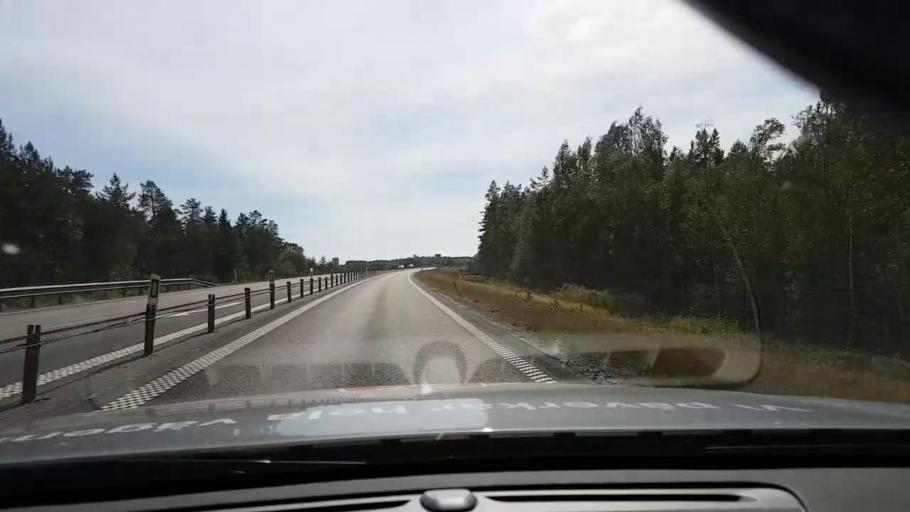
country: SE
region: Vaesternorrland
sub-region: OErnskoeldsviks Kommun
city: Husum
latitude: 63.3718
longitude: 19.1894
